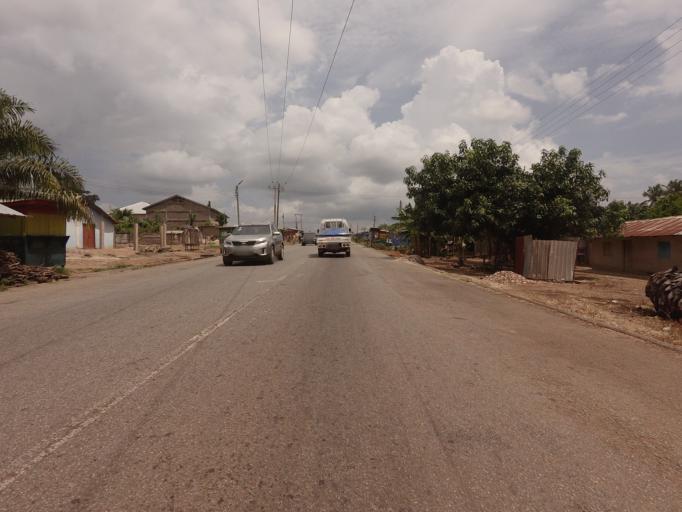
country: GH
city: Akropong
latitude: 6.2589
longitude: 0.1350
